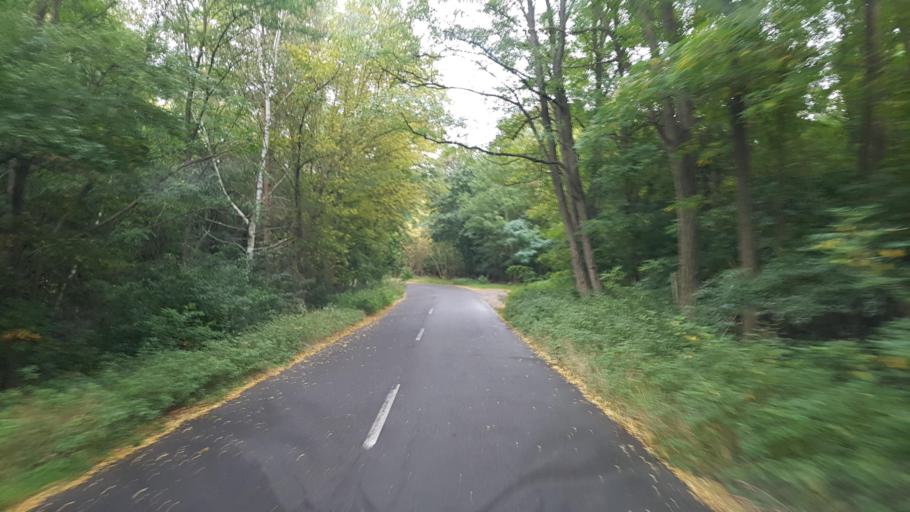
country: DE
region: Brandenburg
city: Zossen
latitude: 52.1623
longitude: 13.4887
